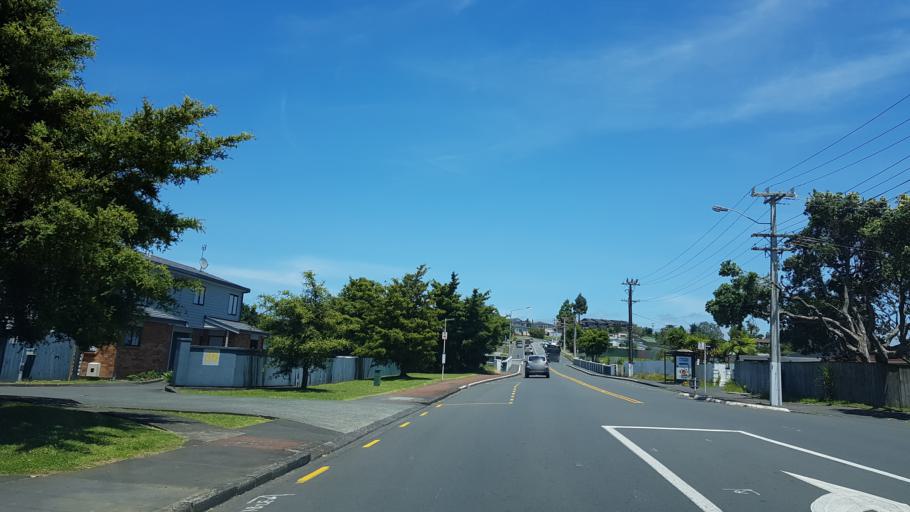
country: NZ
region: Auckland
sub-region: Auckland
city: Waitakere
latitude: -36.9109
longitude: 174.6616
